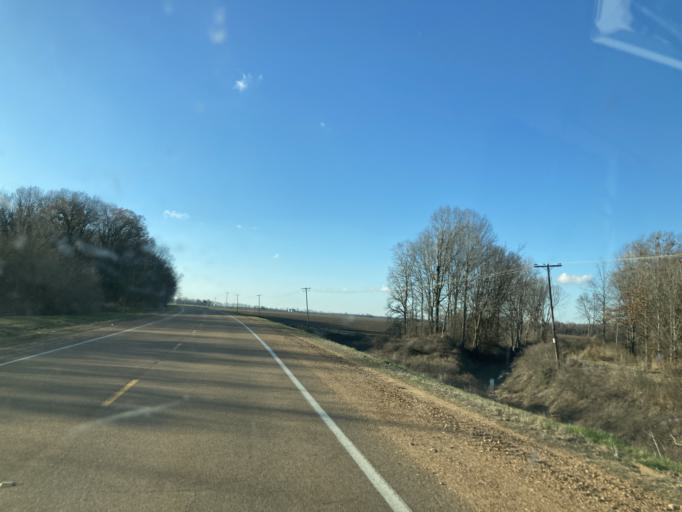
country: US
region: Mississippi
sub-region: Yazoo County
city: Yazoo City
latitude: 32.9242
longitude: -90.5696
